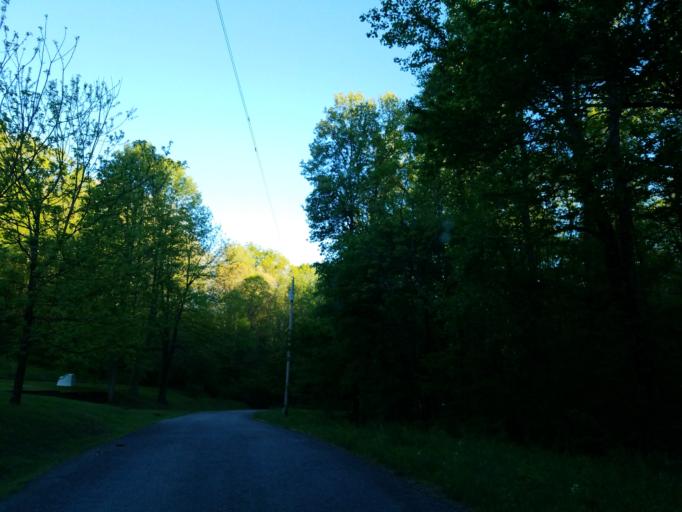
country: US
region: Georgia
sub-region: Union County
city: Blairsville
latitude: 34.7266
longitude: -84.0592
